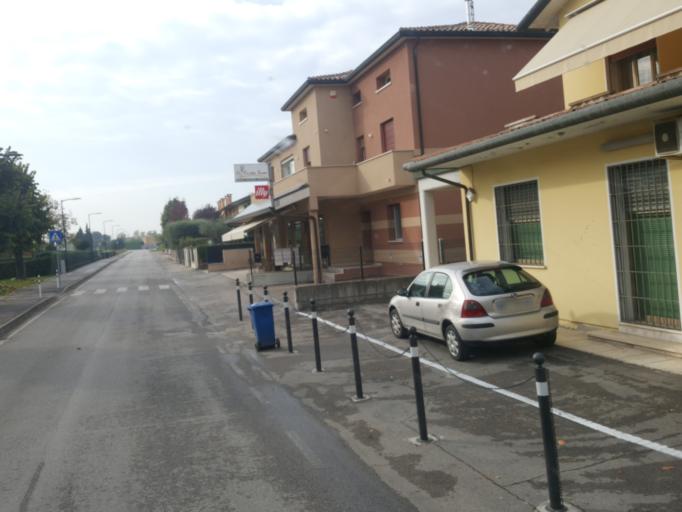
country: IT
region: Veneto
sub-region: Provincia di Treviso
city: Ca' Rainati
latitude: 45.7563
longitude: 11.8481
